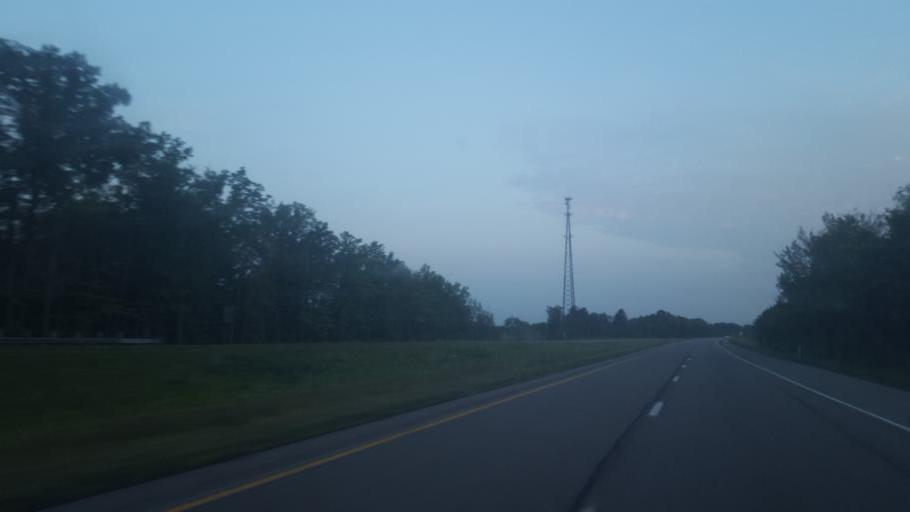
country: US
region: Pennsylvania
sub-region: Crawford County
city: Cochranton
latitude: 41.4587
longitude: -80.1642
